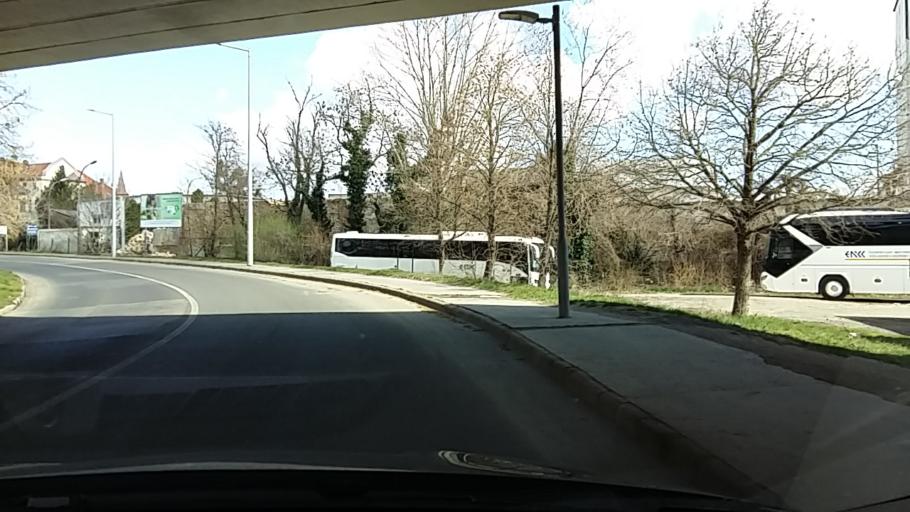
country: HU
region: Baranya
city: Pecs
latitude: 46.0689
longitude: 18.2328
